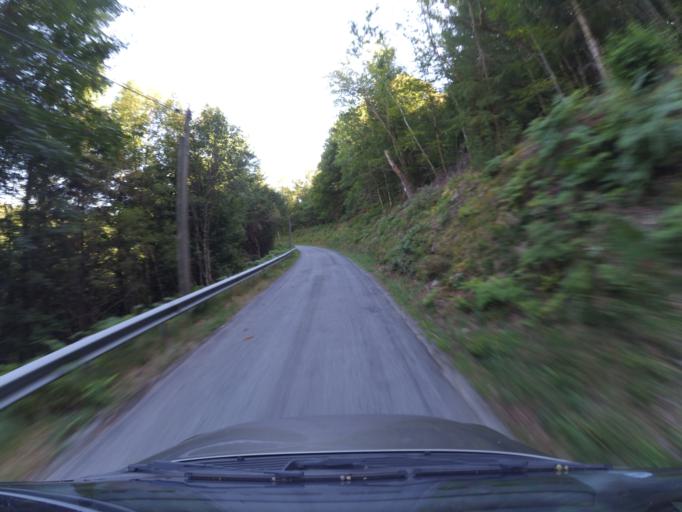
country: FR
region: Limousin
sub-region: Departement de la Correze
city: Bugeat
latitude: 45.6907
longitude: 1.9364
